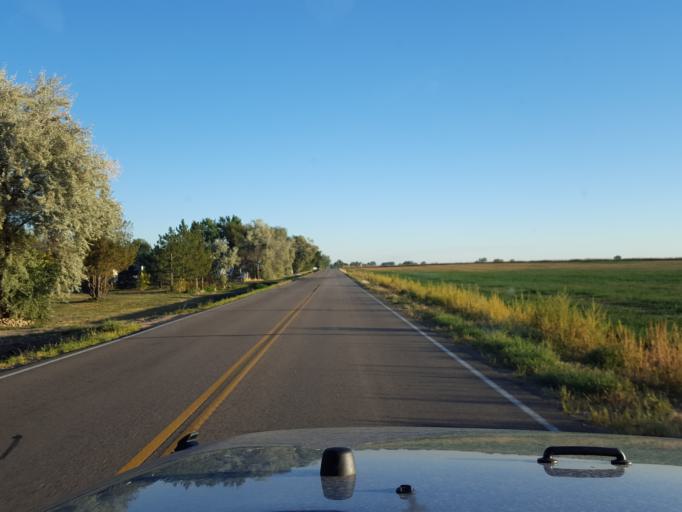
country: US
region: Colorado
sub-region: Boulder County
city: Erie
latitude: 40.0799
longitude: -105.0178
